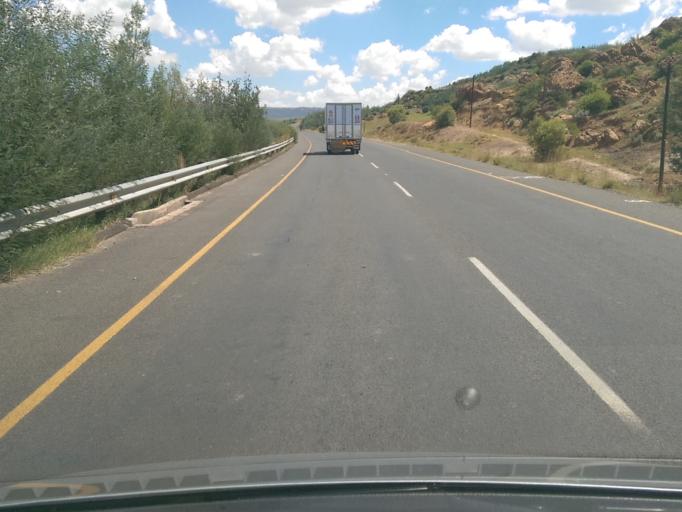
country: LS
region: Maseru
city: Maseru
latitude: -29.3959
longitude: 27.5380
